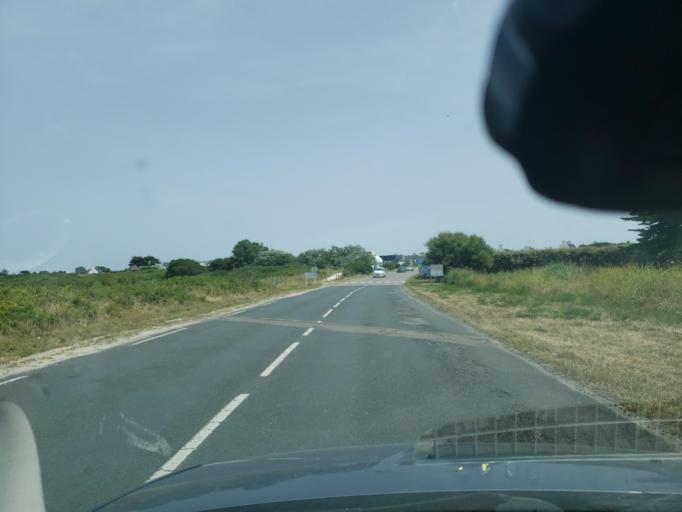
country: FR
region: Brittany
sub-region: Departement du Finistere
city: Guilvinec
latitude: 47.8026
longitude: -4.3001
